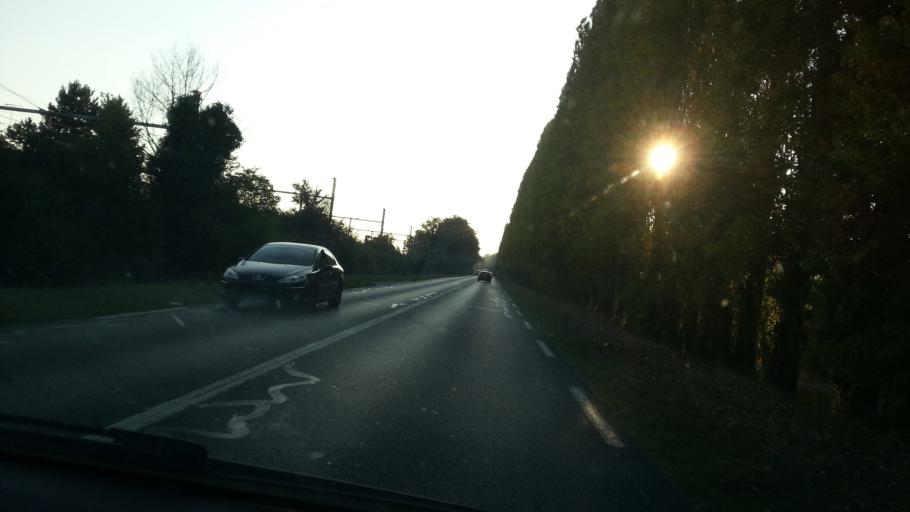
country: FR
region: Picardie
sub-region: Departement de l'Oise
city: Rieux
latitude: 49.2953
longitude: 2.5139
